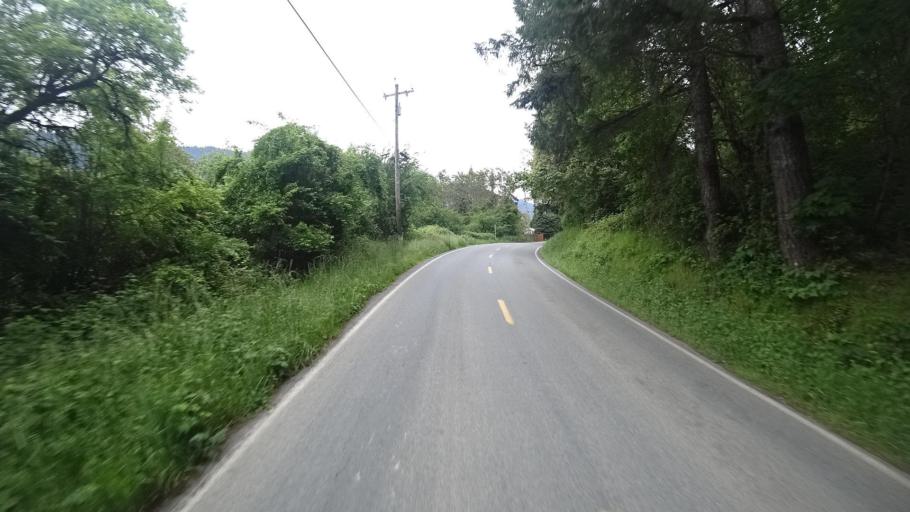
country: US
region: California
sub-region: Humboldt County
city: Willow Creek
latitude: 41.0587
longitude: -123.6900
